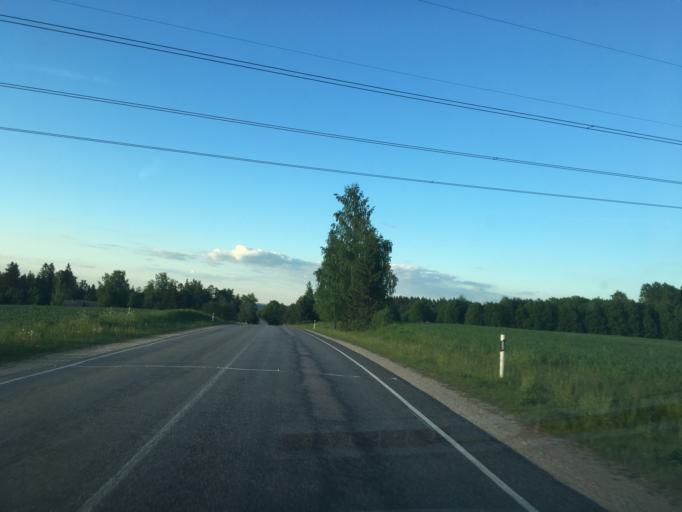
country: EE
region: Tartu
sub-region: Noo vald
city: Noo
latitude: 58.2197
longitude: 26.6264
